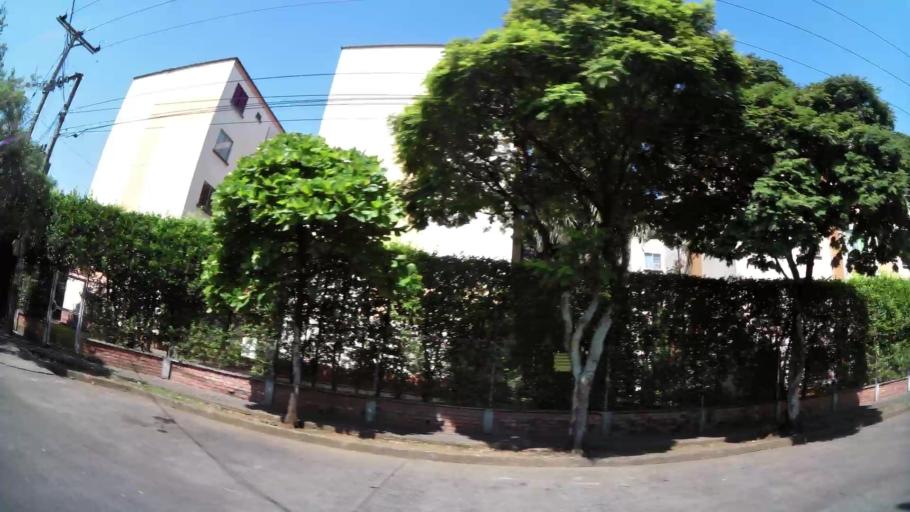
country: CO
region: Valle del Cauca
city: Cali
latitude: 3.4002
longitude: -76.5249
